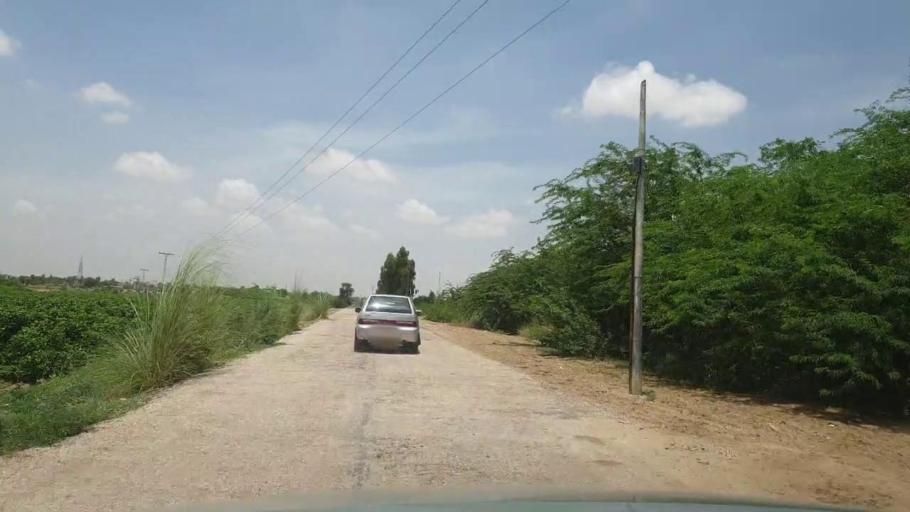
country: PK
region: Sindh
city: Kot Diji
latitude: 27.1552
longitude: 68.9745
